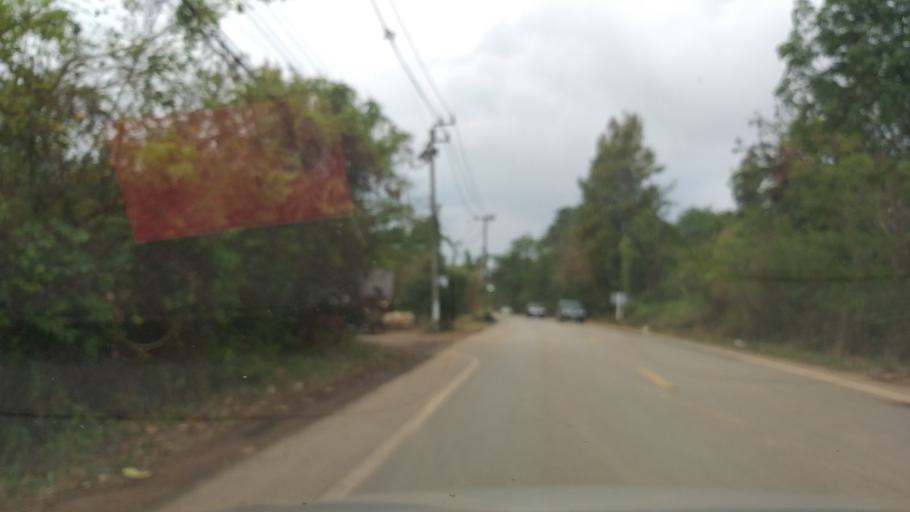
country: TH
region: Trat
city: Laem Ngop
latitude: 12.1892
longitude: 102.2969
